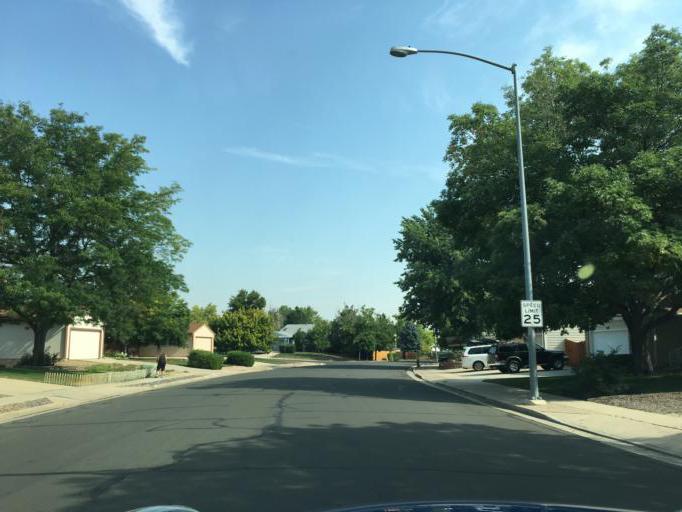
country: US
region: Colorado
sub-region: Adams County
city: Westminster
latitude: 39.8315
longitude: -105.0589
